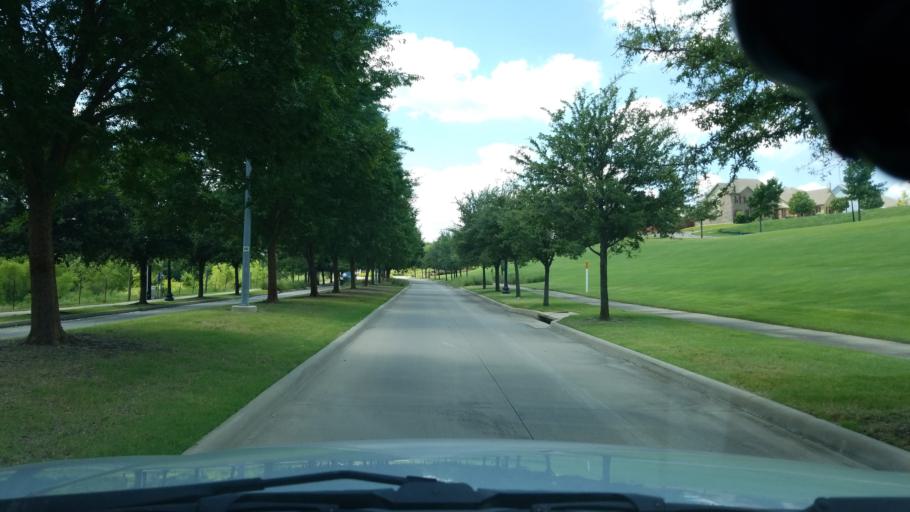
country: US
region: Texas
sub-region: Dallas County
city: Duncanville
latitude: 32.7009
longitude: -96.9430
